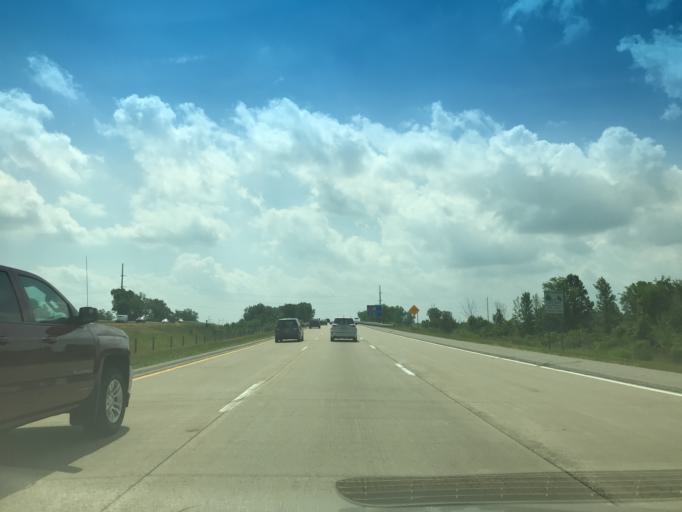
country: US
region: Michigan
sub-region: Eaton County
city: Dimondale
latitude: 42.6863
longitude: -84.6647
